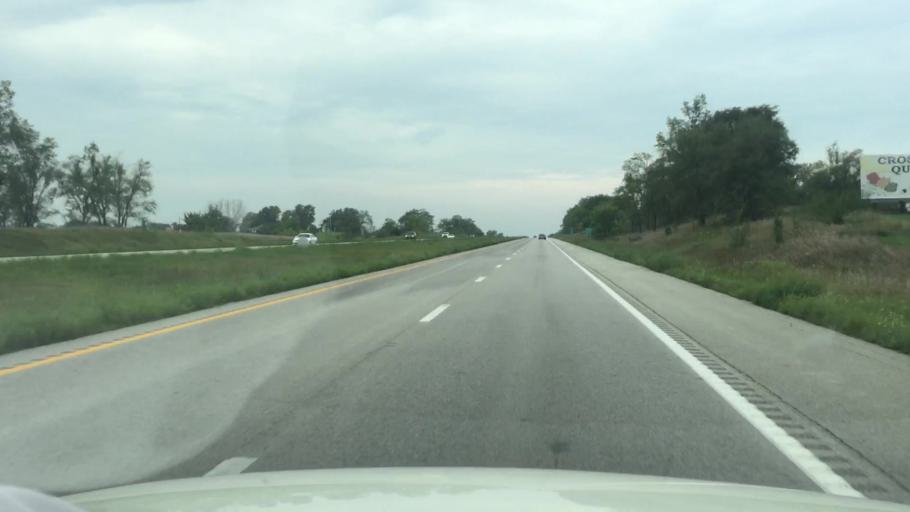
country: US
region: Missouri
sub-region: Clinton County
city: Cameron
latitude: 39.7914
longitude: -94.2049
